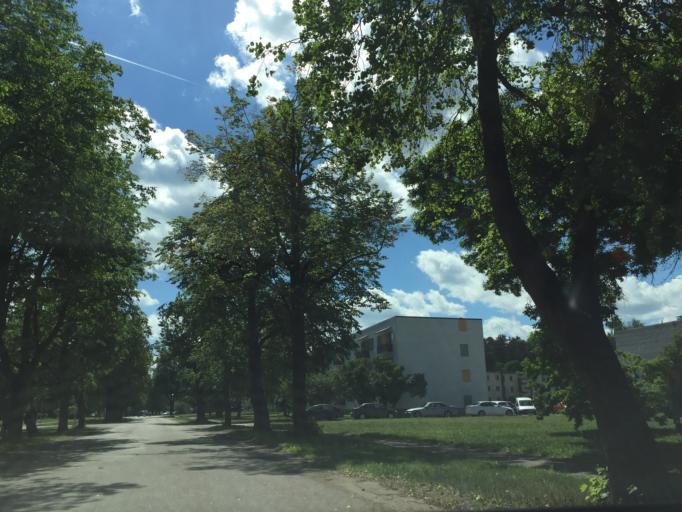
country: LV
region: Babite
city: Pinki
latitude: 56.8816
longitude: 23.9446
